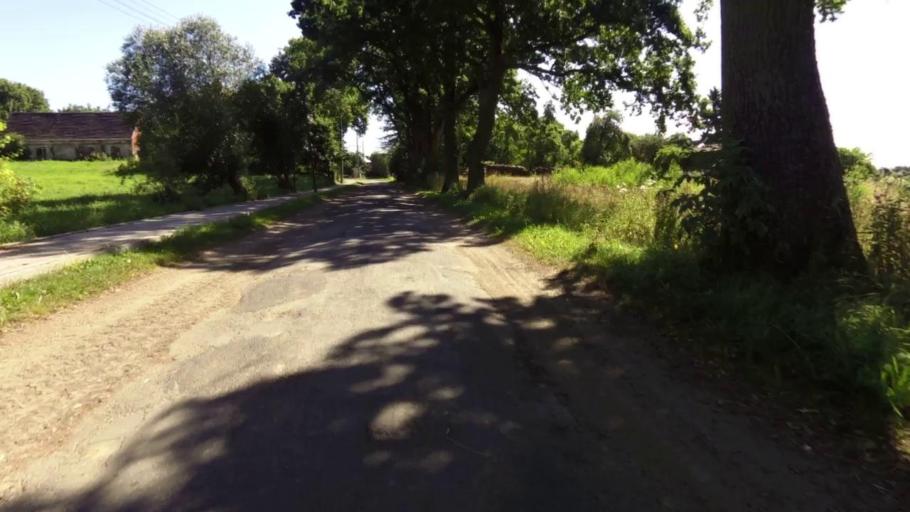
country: PL
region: West Pomeranian Voivodeship
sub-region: Powiat drawski
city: Zlocieniec
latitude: 53.5216
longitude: 16.0621
